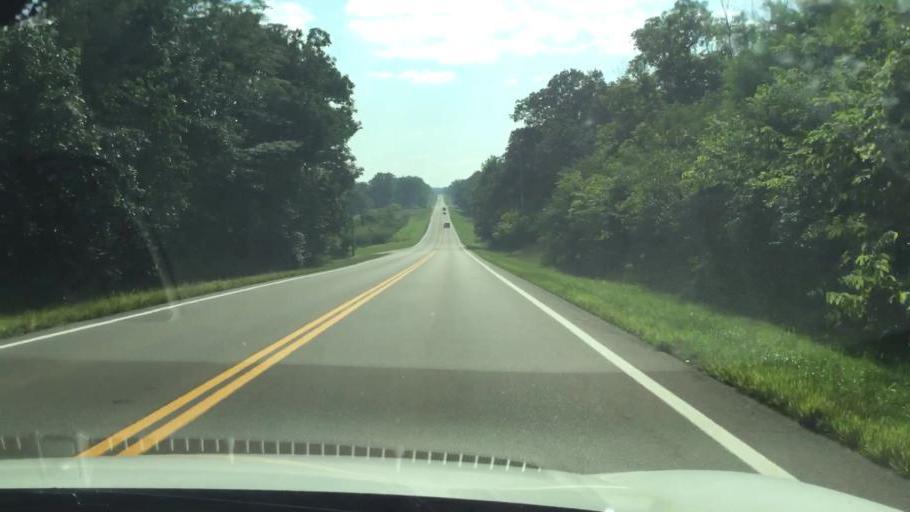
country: US
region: Ohio
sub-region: Clark County
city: Northridge
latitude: 40.0133
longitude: -83.6940
